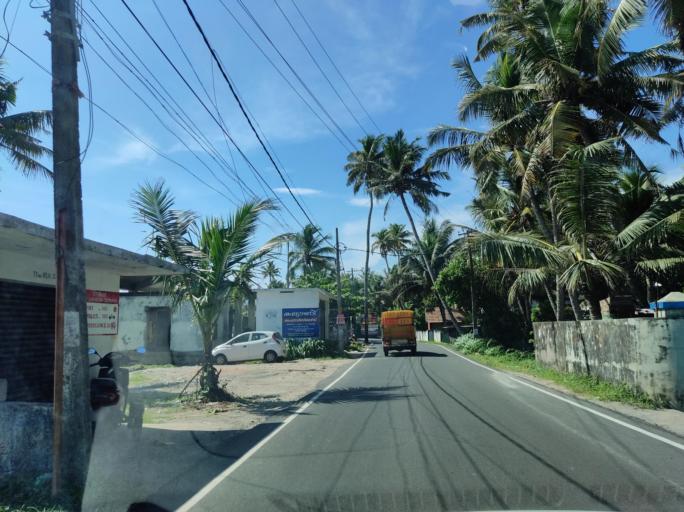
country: IN
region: Kerala
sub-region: Alappuzha
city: Kayankulam
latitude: 9.2578
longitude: 76.4076
